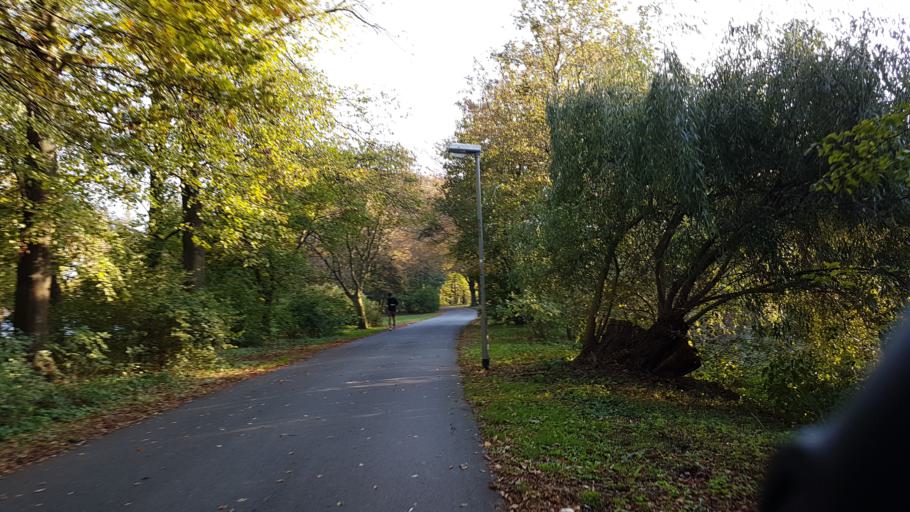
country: DE
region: Lower Saxony
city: Hannover
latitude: 52.3599
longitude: 9.7355
